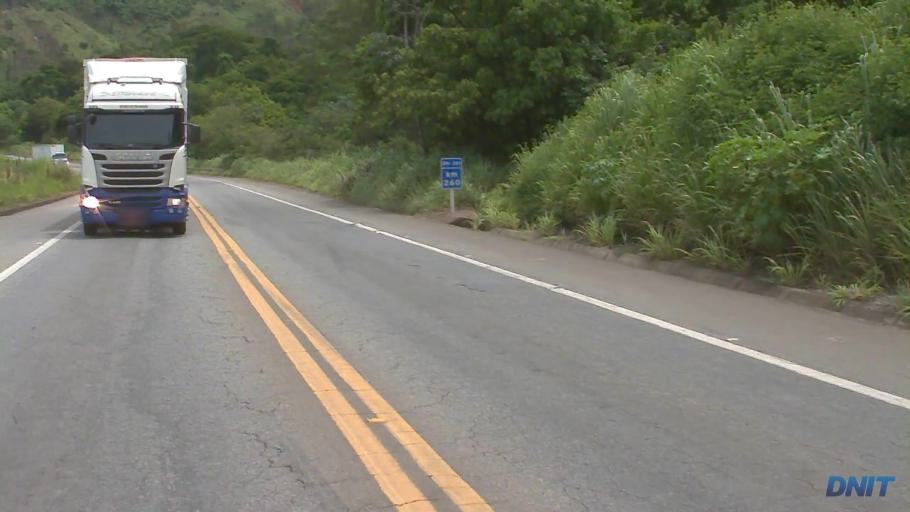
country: BR
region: Minas Gerais
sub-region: Coronel Fabriciano
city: Coronel Fabriciano
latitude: -19.5309
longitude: -42.6061
